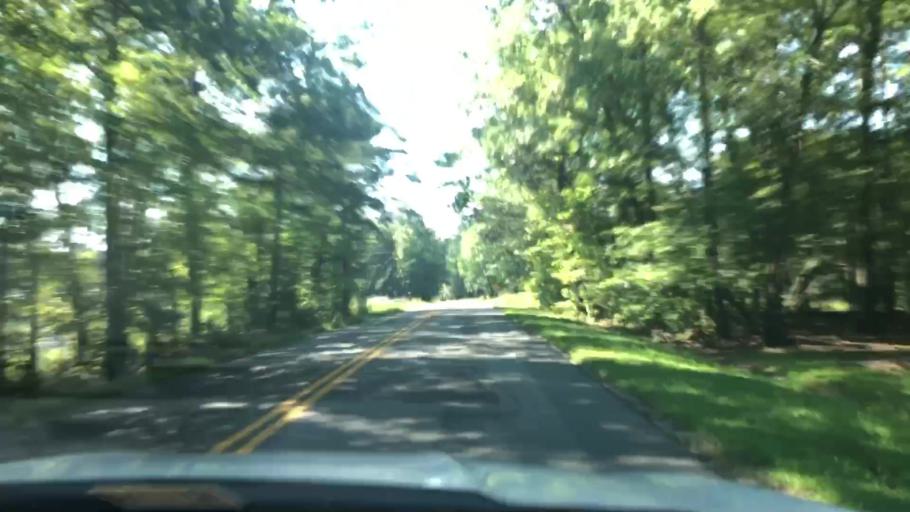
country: US
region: Virginia
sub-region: New Kent County
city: New Kent
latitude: 37.4211
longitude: -76.9132
